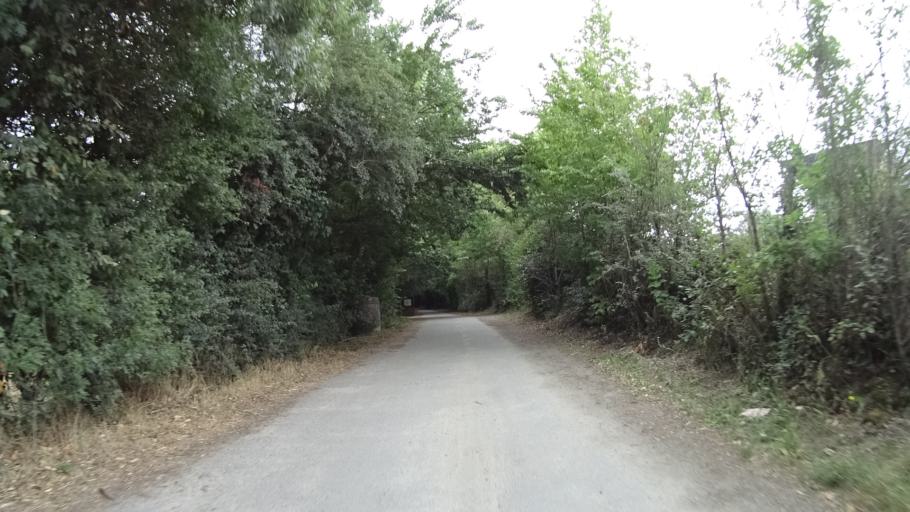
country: FR
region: Pays de la Loire
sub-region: Departement de la Loire-Atlantique
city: Thouare-sur-Loire
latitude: 47.2479
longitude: -1.4537
